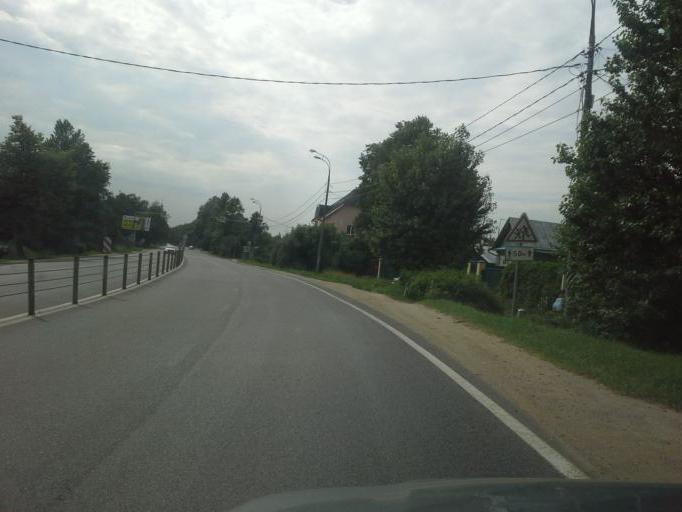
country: RU
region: Moskovskaya
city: Zhavoronki
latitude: 55.6583
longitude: 37.1290
